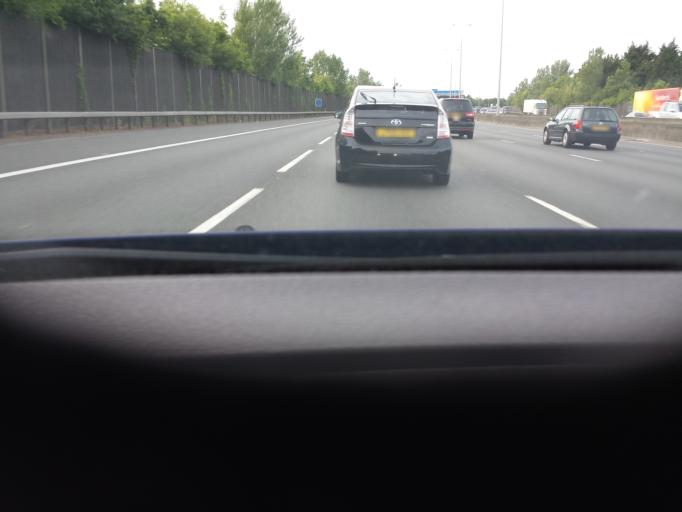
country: GB
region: England
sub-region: Surrey
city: Egham
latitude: 51.4268
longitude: -0.5411
